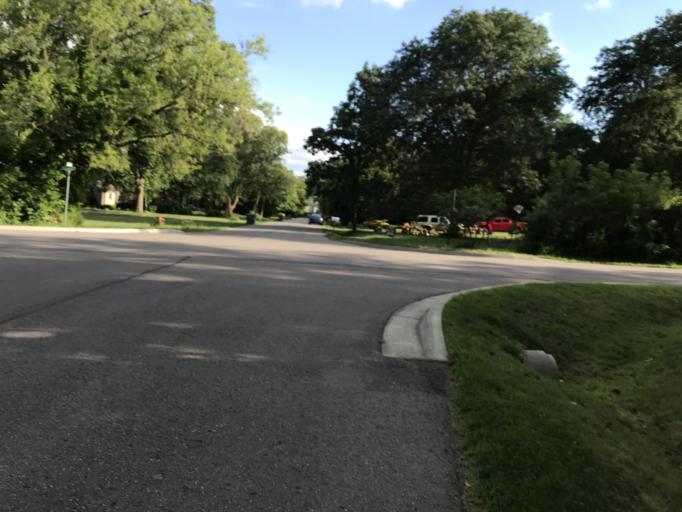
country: US
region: Michigan
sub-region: Oakland County
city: Farmington
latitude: 42.4658
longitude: -83.3500
